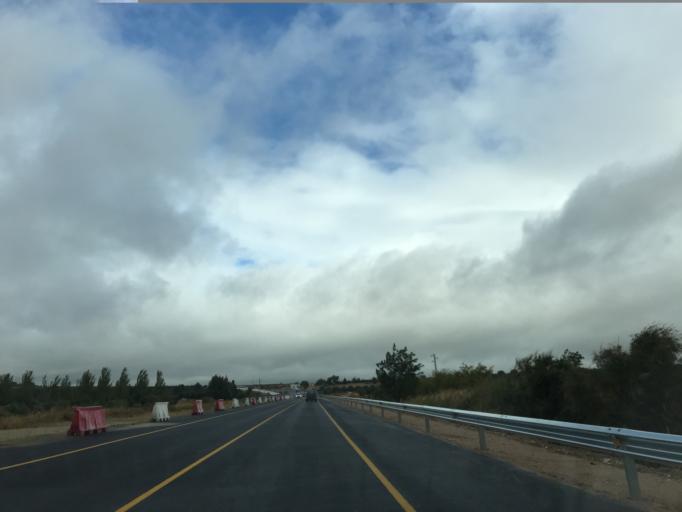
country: ES
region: Andalusia
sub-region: Provincia de Jaen
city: Ubeda
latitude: 38.0196
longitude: -3.4083
